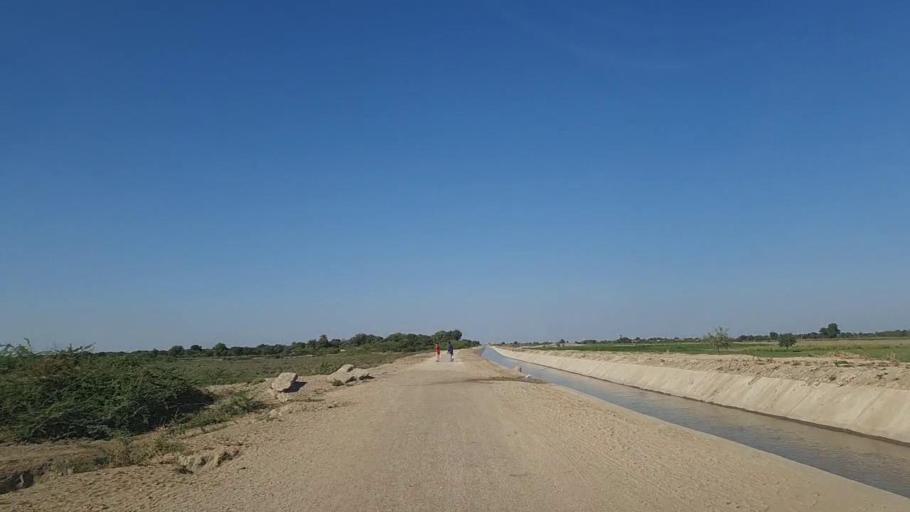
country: PK
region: Sindh
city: Kunri
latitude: 25.2267
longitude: 69.5149
